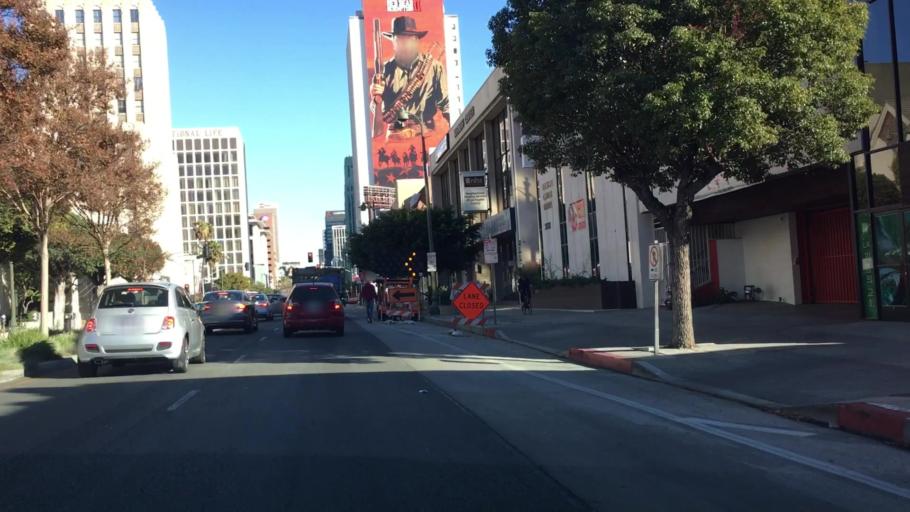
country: US
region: California
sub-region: Los Angeles County
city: Hollywood
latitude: 34.0617
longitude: -118.3128
